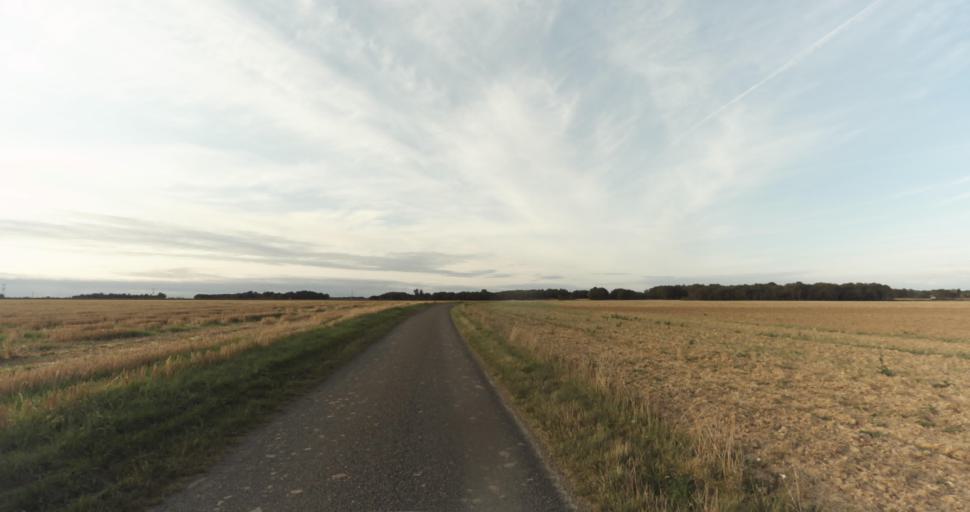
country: FR
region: Haute-Normandie
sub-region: Departement de l'Eure
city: Saint-Germain-sur-Avre
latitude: 48.8323
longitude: 1.2675
